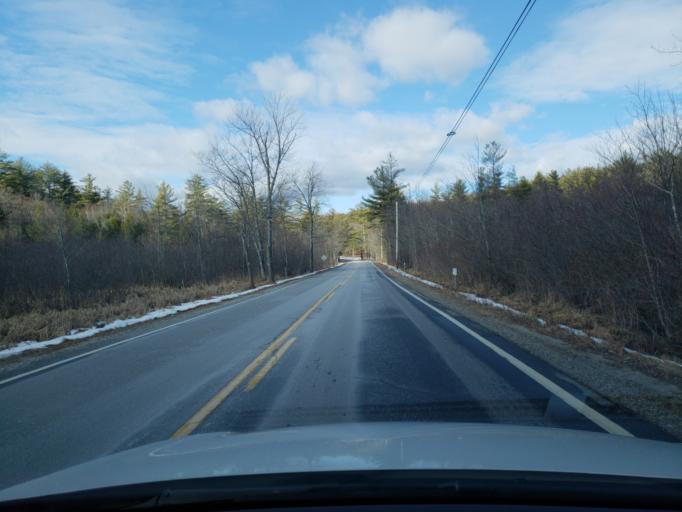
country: US
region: New Hampshire
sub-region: Hillsborough County
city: New Boston
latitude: 42.9976
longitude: -71.7539
